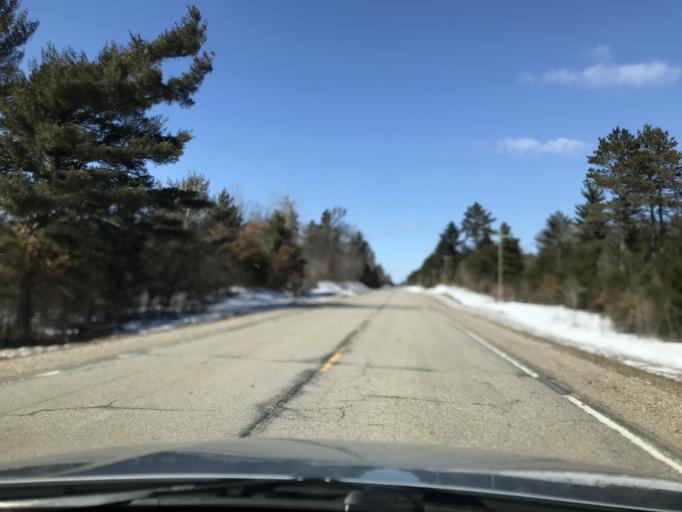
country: US
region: Wisconsin
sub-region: Marinette County
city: Niagara
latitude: 45.3862
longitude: -88.0996
